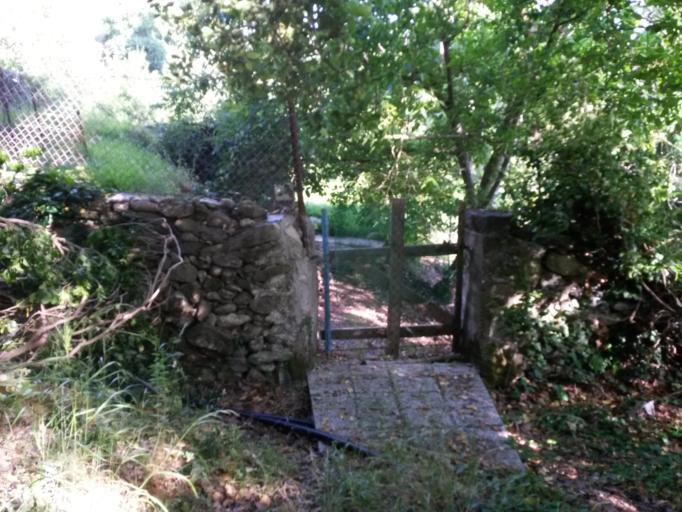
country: GR
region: North Aegean
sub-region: Nomos Lesvou
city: Agiasos
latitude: 39.1092
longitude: 26.3950
